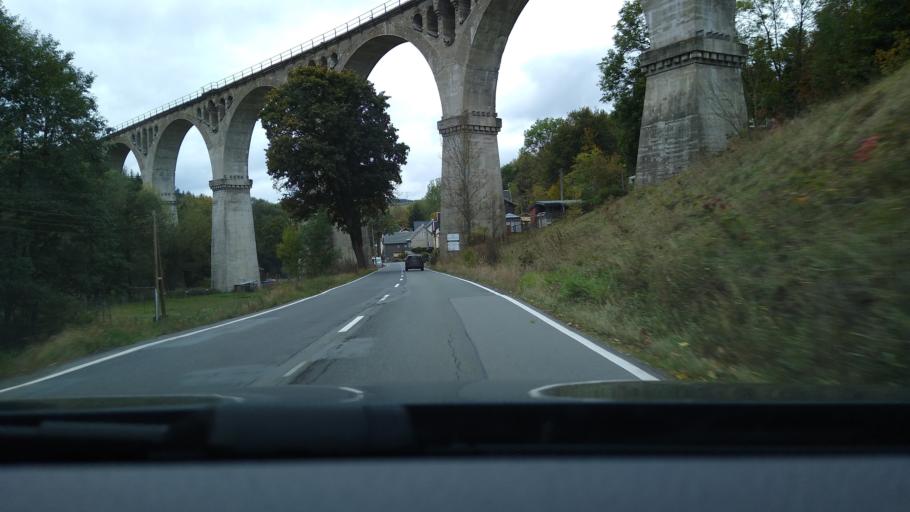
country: DE
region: Thuringia
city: Schmiedefeld
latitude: 50.5254
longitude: 11.2038
